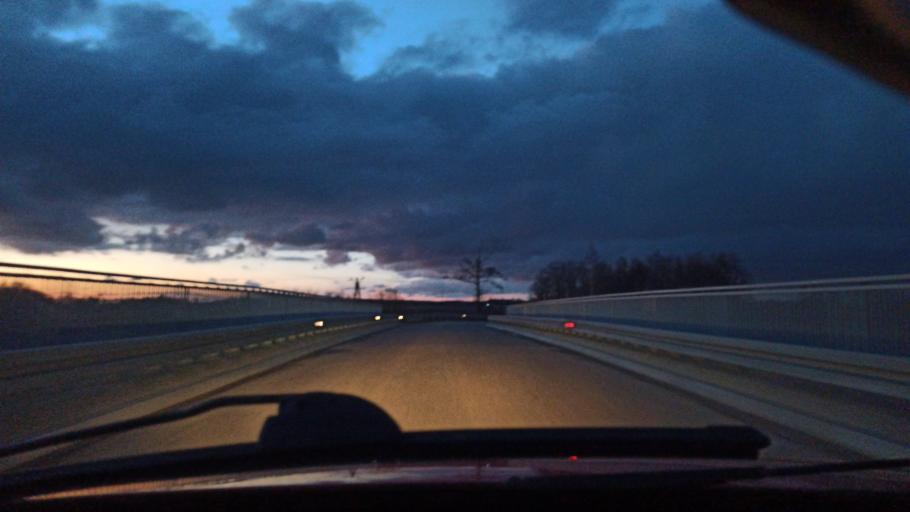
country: PL
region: Warmian-Masurian Voivodeship
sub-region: Powiat elblaski
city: Gronowo Gorne
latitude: 54.1726
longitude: 19.5355
